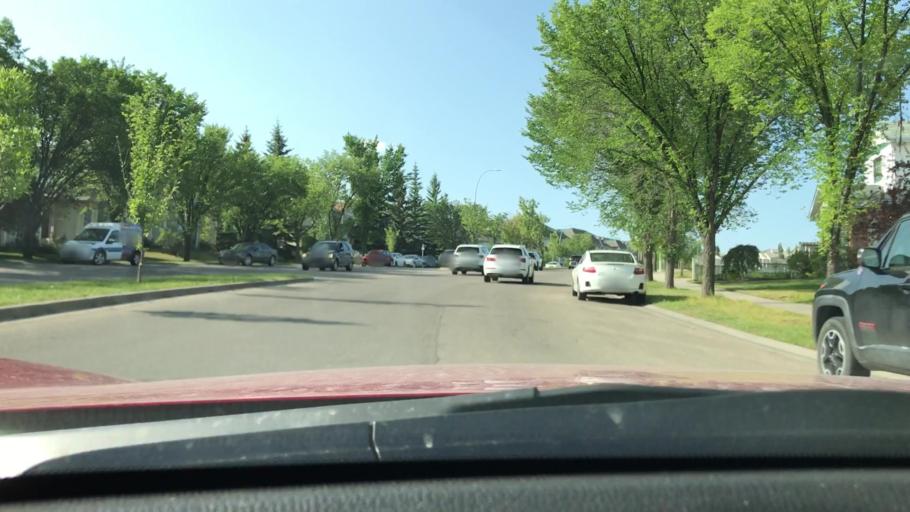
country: CA
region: Alberta
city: Calgary
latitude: 51.0219
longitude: -114.1841
